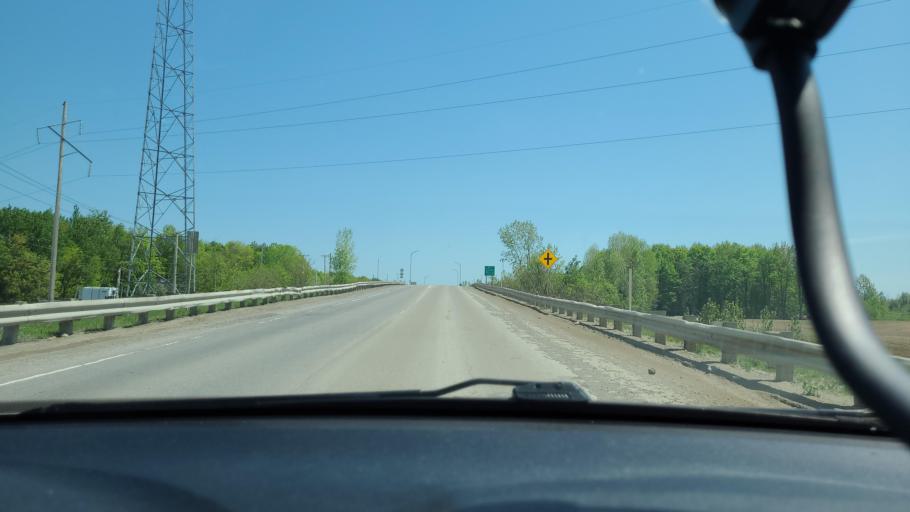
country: CA
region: Quebec
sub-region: Laurentides
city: Saint-Colomban
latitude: 45.6771
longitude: -74.1867
